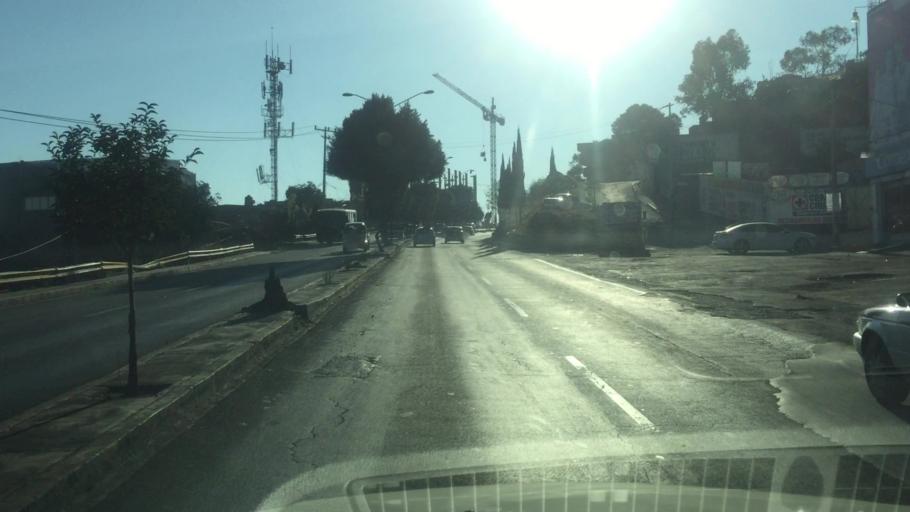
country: MX
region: Mexico City
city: Tlalpan
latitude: 19.2792
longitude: -99.2118
